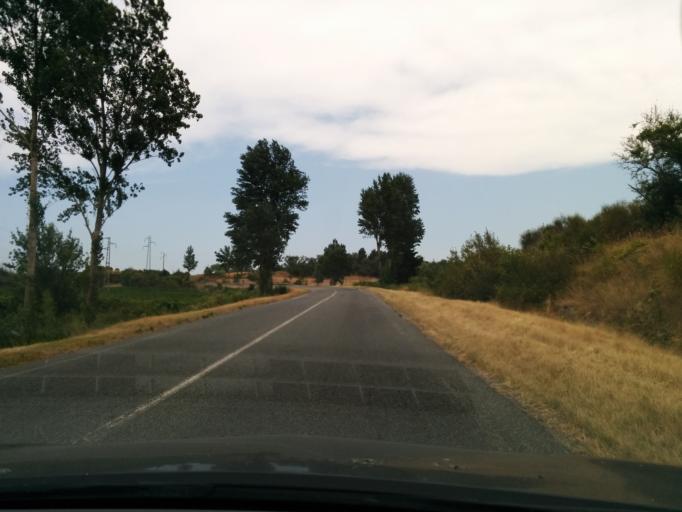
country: FR
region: Languedoc-Roussillon
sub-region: Departement de l'Aude
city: Cazilhac
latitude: 43.2000
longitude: 2.3680
